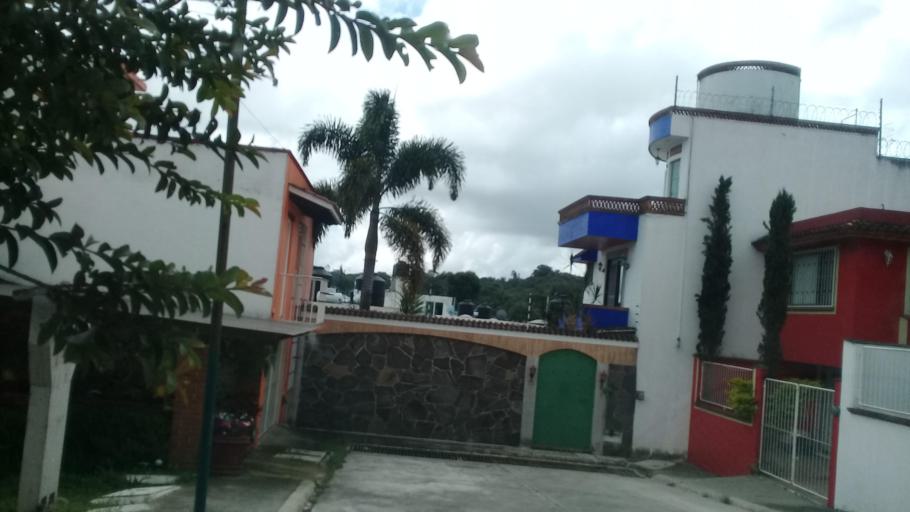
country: MX
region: Veracruz
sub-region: Xalapa
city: Xalapa de Enriquez
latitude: 19.5065
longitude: -96.9219
